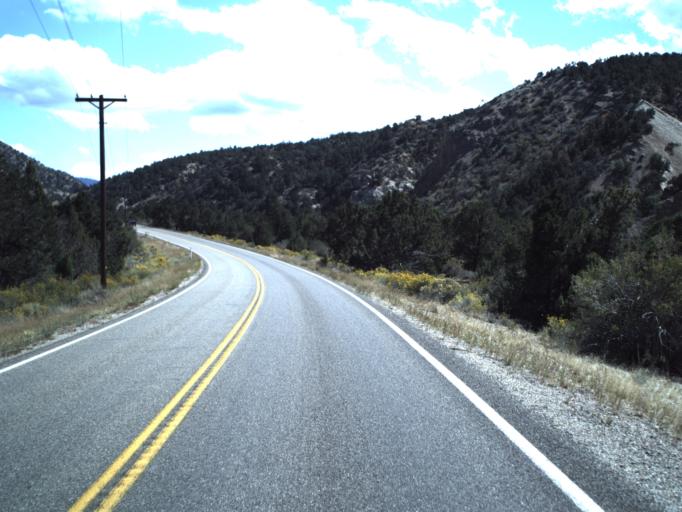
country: US
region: Utah
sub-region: Iron County
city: Cedar City
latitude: 37.6675
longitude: -113.0103
